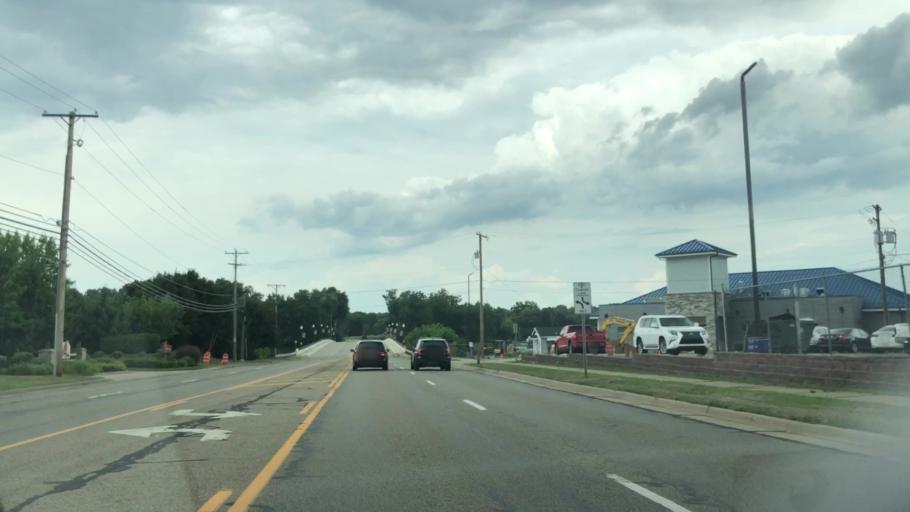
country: US
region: Ohio
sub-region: Summit County
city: Portage Lakes
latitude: 40.9853
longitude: -81.5219
